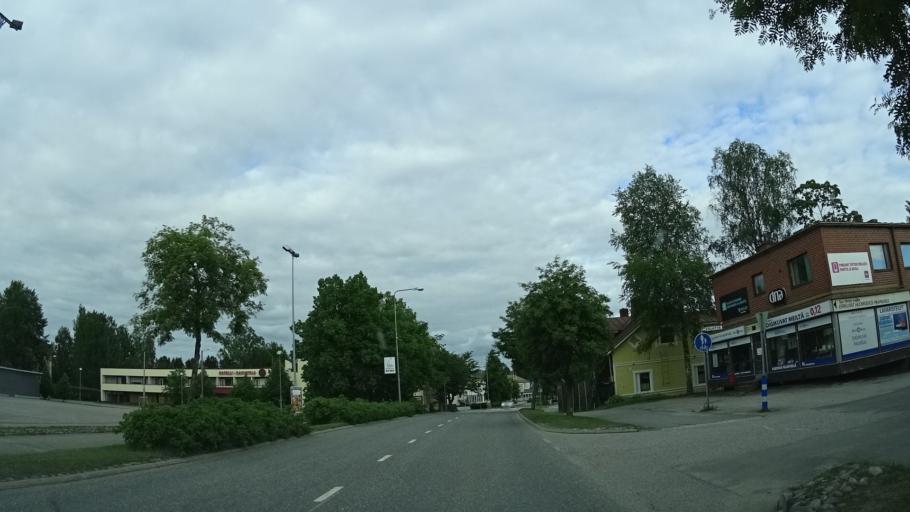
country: FI
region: Paijanne Tavastia
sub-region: Lahti
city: Sysmae
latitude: 61.5019
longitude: 25.6882
